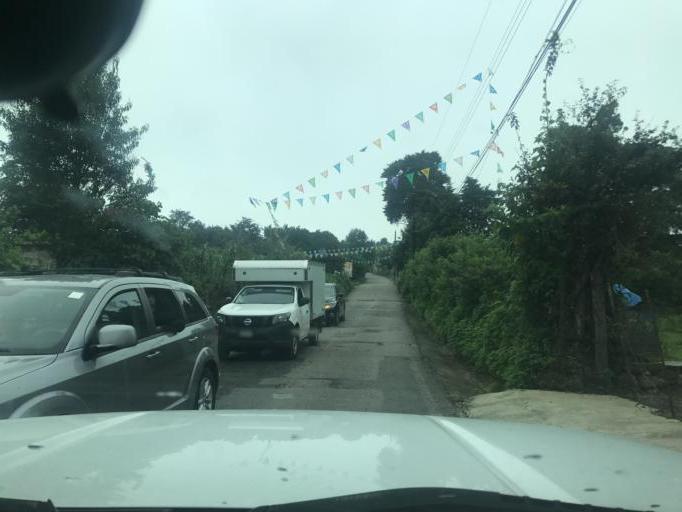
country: MX
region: Morelos
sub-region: Ocuituco
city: Huepalcalco (San Miguel)
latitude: 18.9049
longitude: -98.7509
